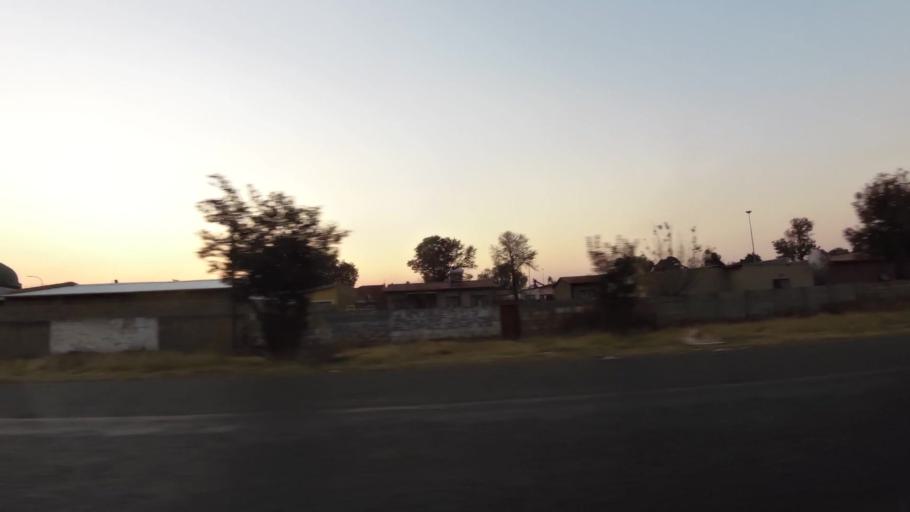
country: ZA
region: Gauteng
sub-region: City of Johannesburg Metropolitan Municipality
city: Soweto
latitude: -26.2932
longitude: 27.8773
